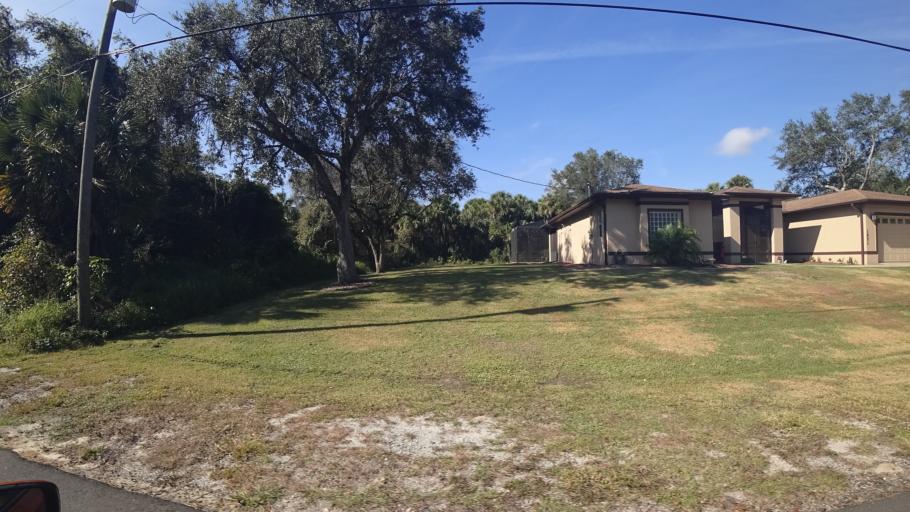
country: US
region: Florida
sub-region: Charlotte County
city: Port Charlotte
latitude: 27.0595
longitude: -82.1202
